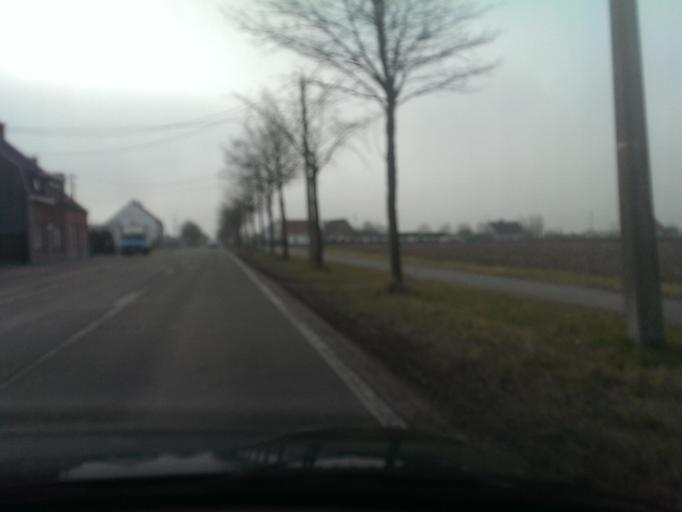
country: BE
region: Flanders
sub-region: Provincie West-Vlaanderen
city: Ledegem
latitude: 50.8710
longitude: 3.1111
